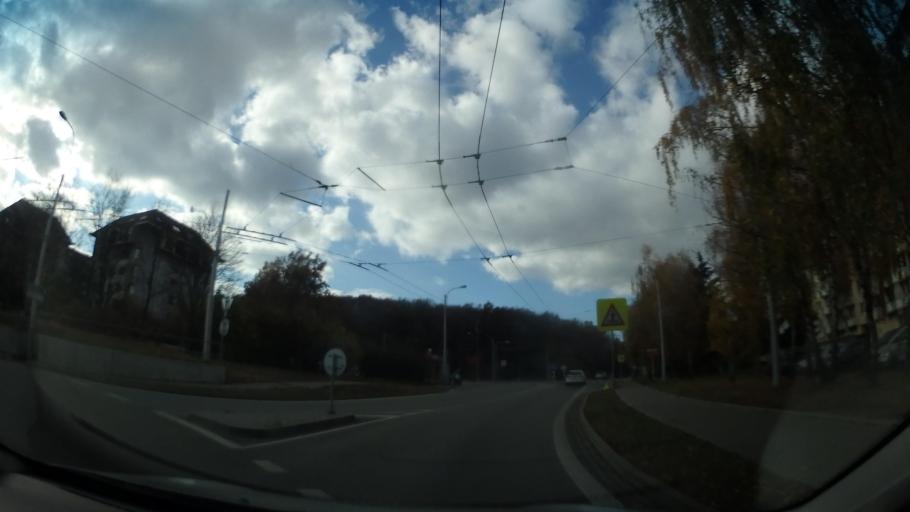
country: CZ
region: South Moravian
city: Troubsko
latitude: 49.1964
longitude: 16.5322
